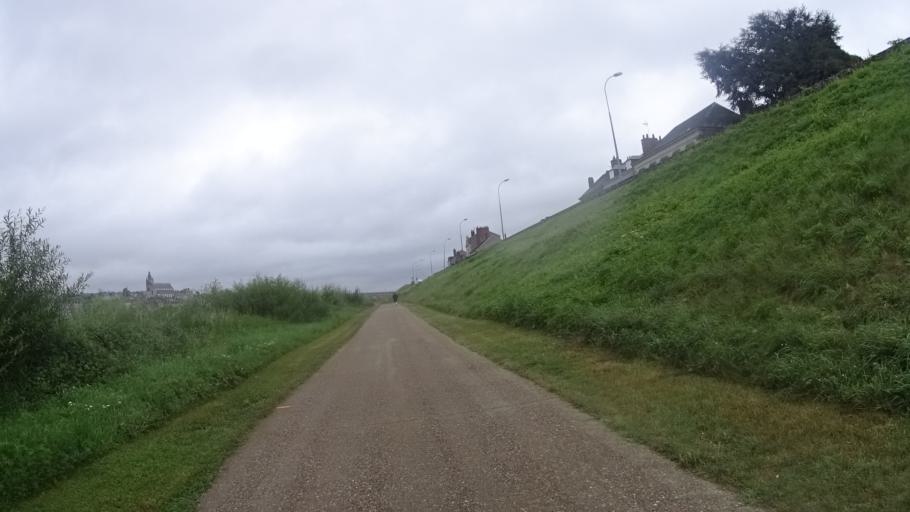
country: FR
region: Centre
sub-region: Departement du Loir-et-Cher
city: Blois
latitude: 47.5795
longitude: 1.3320
